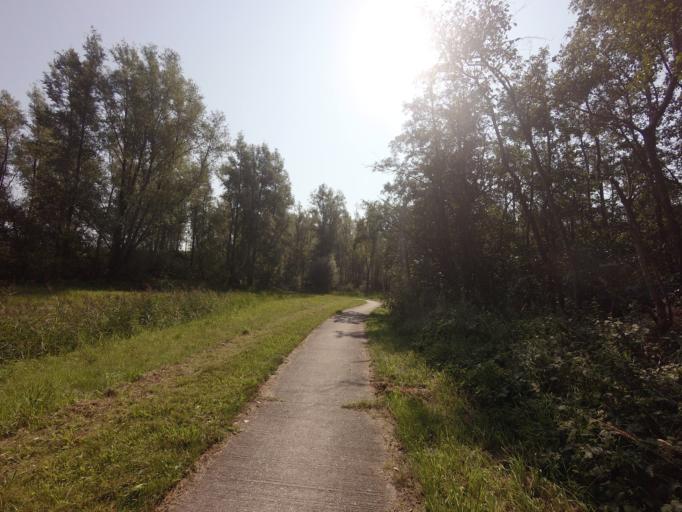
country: NL
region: Groningen
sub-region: Gemeente De Marne
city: Ulrum
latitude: 53.3919
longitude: 6.2566
